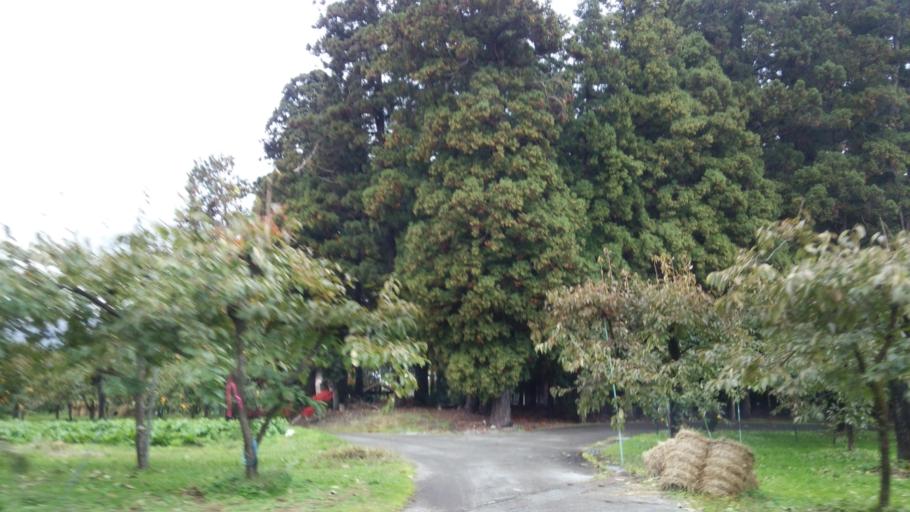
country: JP
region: Fukushima
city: Kitakata
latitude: 37.4603
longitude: 139.9353
